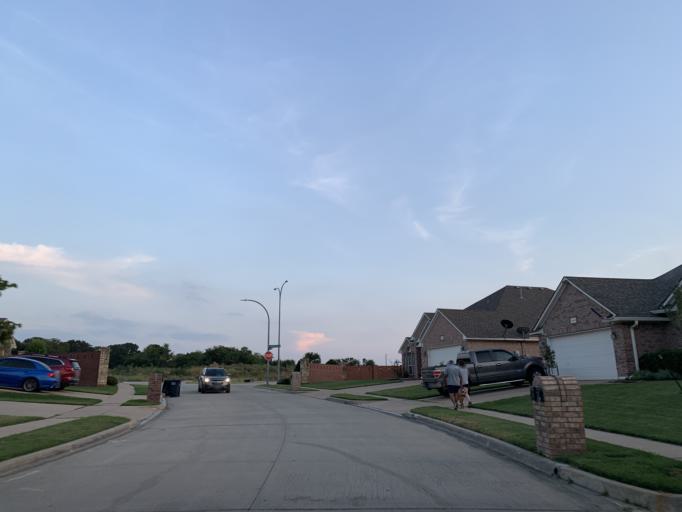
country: US
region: Texas
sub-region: Tarrant County
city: Keller
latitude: 32.9558
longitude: -97.2765
